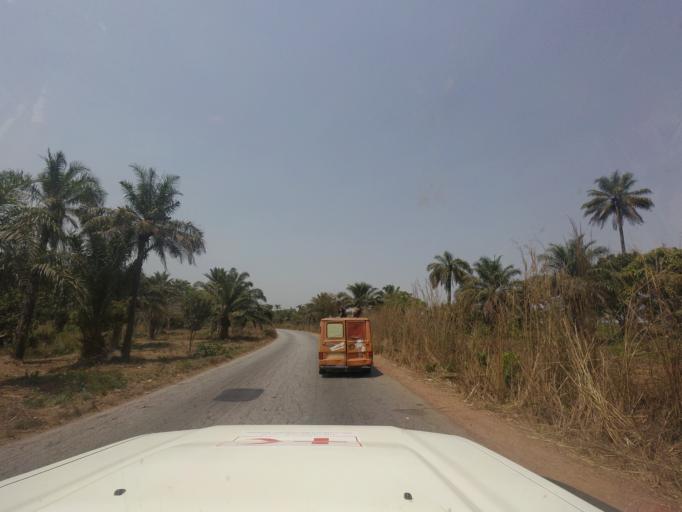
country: GN
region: Kindia
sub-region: Kindia
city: Kindia
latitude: 9.9475
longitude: -12.9586
